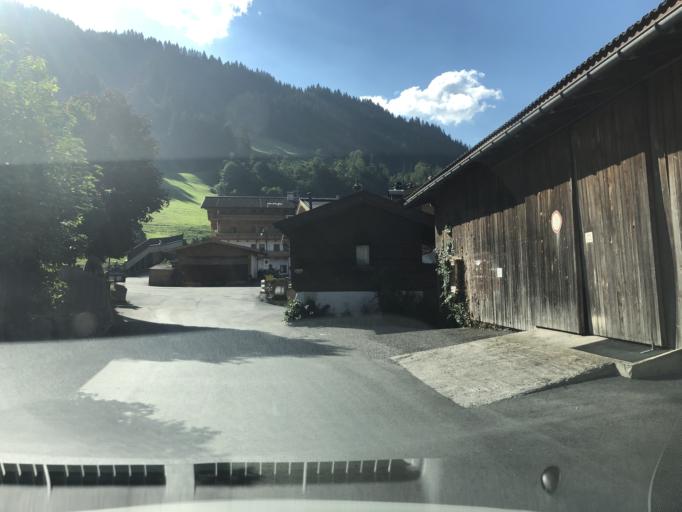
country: AT
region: Tyrol
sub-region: Politischer Bezirk Kitzbuhel
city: Kirchberg in Tirol
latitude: 47.3824
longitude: 12.3099
